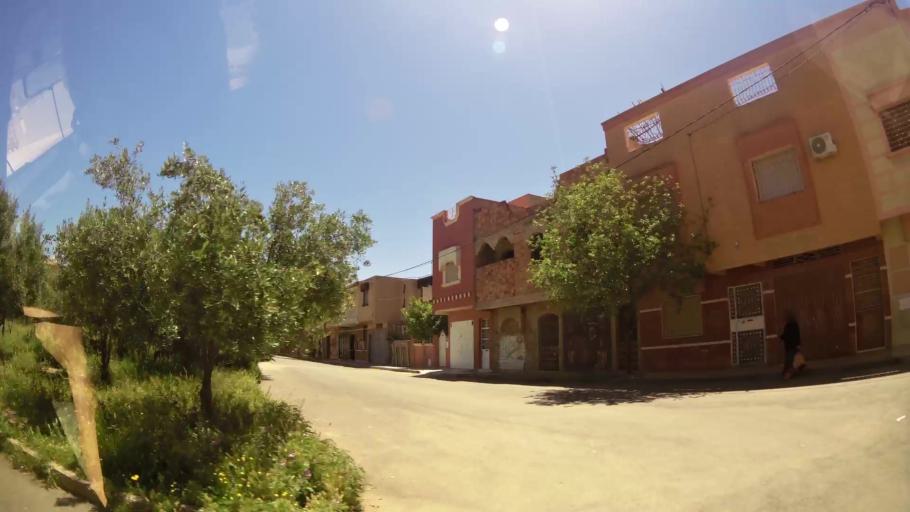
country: MA
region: Oriental
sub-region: Oujda-Angad
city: Oujda
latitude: 34.6702
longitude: -1.8888
